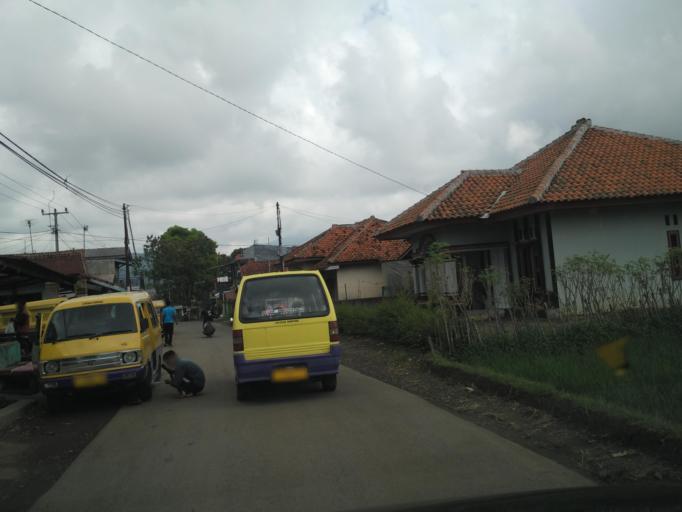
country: ID
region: West Java
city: Ciranjang-hilir
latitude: -6.7332
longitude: 107.0903
